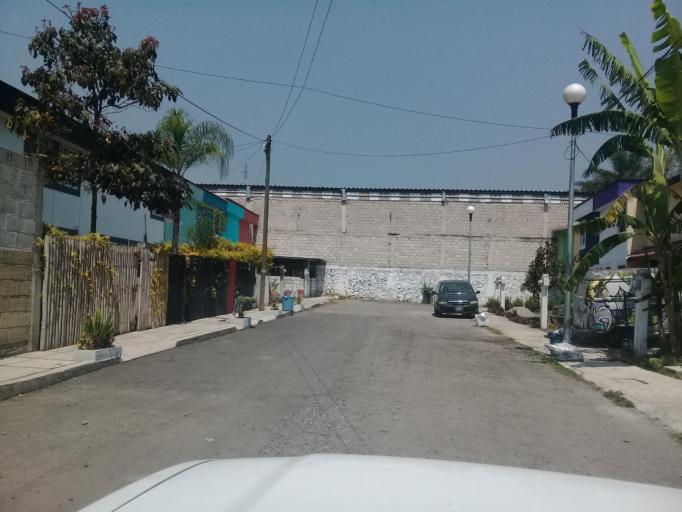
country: MX
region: Veracruz
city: Ixtac Zoquitlan
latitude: 18.8584
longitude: -97.0632
